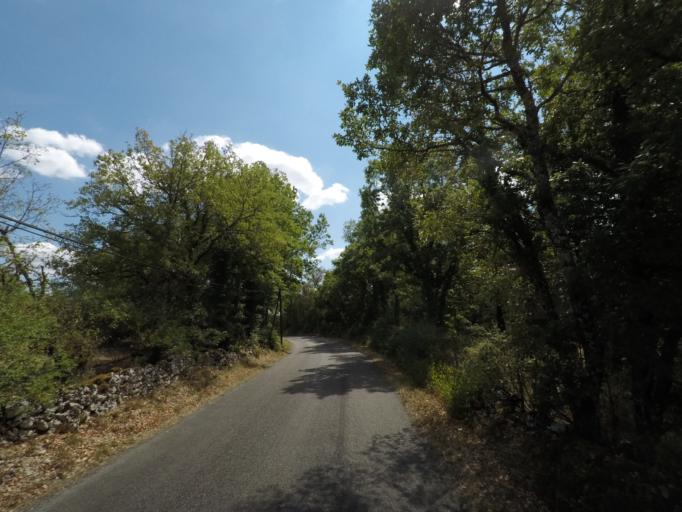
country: FR
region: Midi-Pyrenees
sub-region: Departement du Lot
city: Cajarc
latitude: 44.5649
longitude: 1.6713
